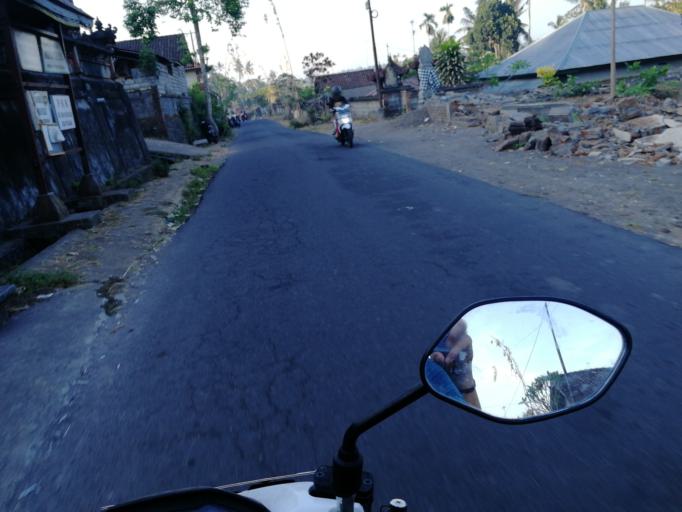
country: ID
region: Bali
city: Tistagede
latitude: -8.3885
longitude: 115.6159
